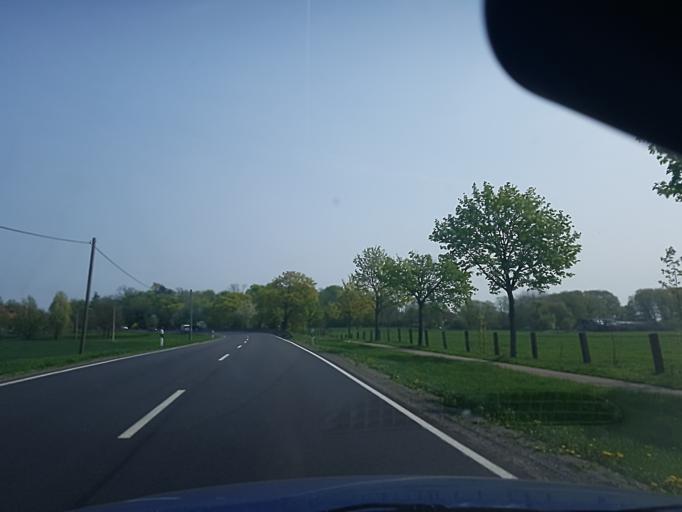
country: DE
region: Saxony
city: Beilrode
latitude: 51.5783
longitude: 13.0370
